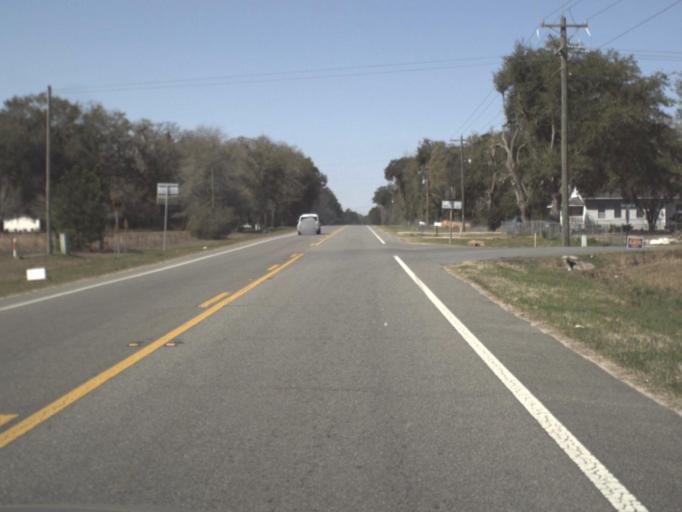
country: US
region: Florida
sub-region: Gadsden County
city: Quincy
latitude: 30.5922
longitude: -84.5119
